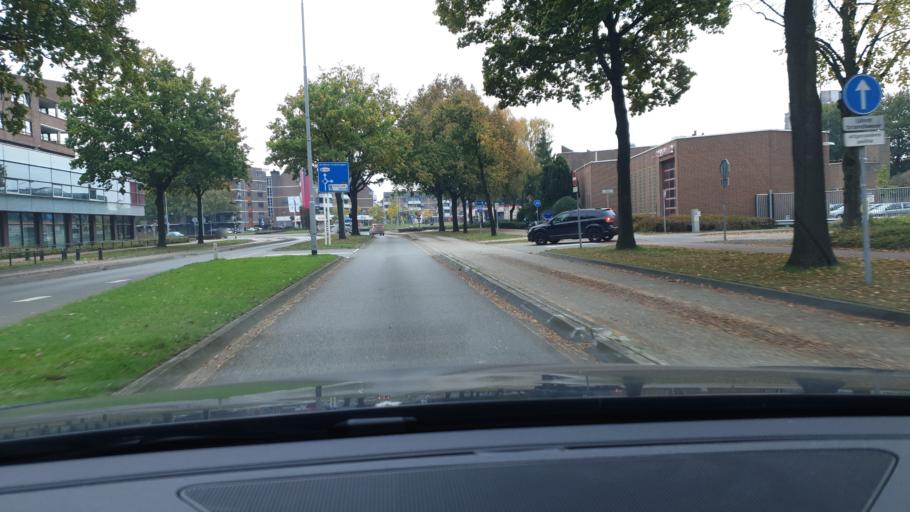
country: NL
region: North Brabant
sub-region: Gemeente Veldhoven
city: Veldhoven
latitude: 51.4232
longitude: 5.4045
